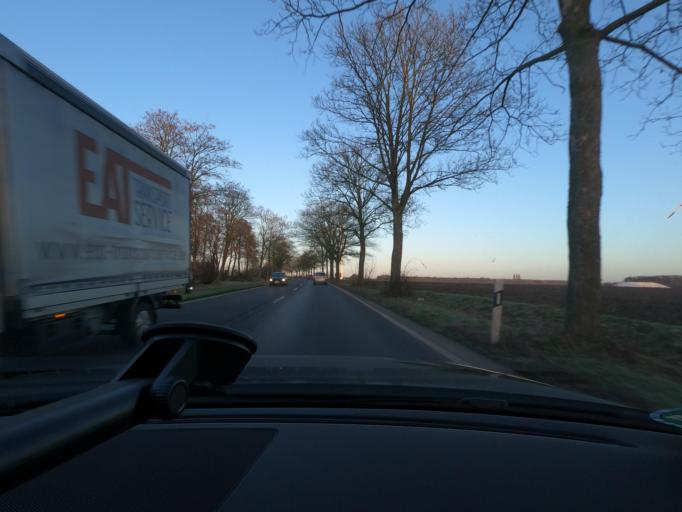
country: DE
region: North Rhine-Westphalia
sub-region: Regierungsbezirk Dusseldorf
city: Wachtendonk
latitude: 51.3907
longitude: 6.3768
